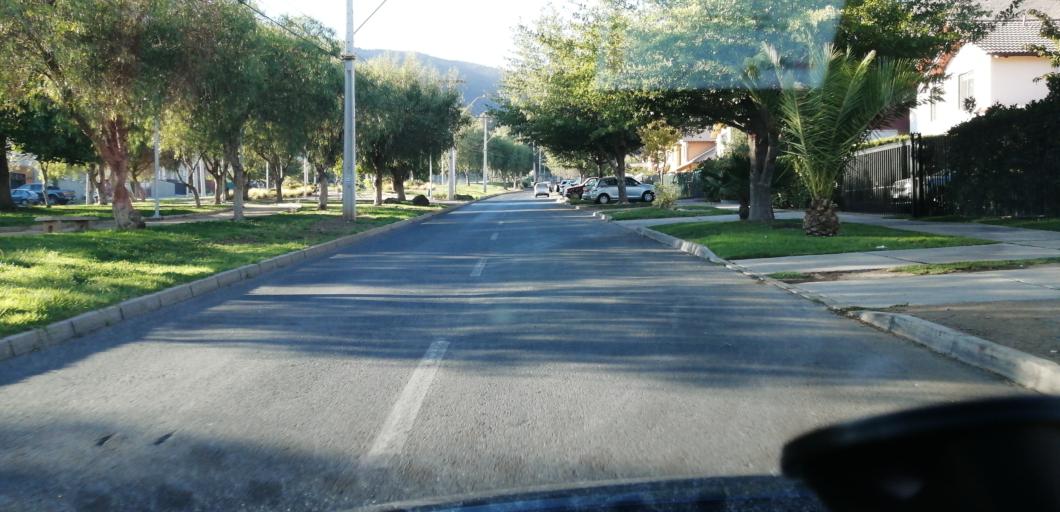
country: CL
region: Santiago Metropolitan
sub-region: Provincia de Santiago
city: Lo Prado
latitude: -33.4549
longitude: -70.8471
